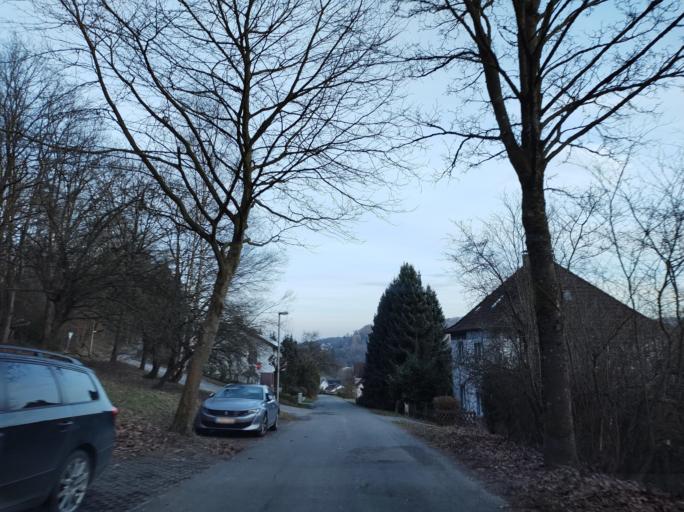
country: DE
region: North Rhine-Westphalia
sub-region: Regierungsbezirk Detmold
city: Detmold
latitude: 51.8951
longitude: 8.8637
